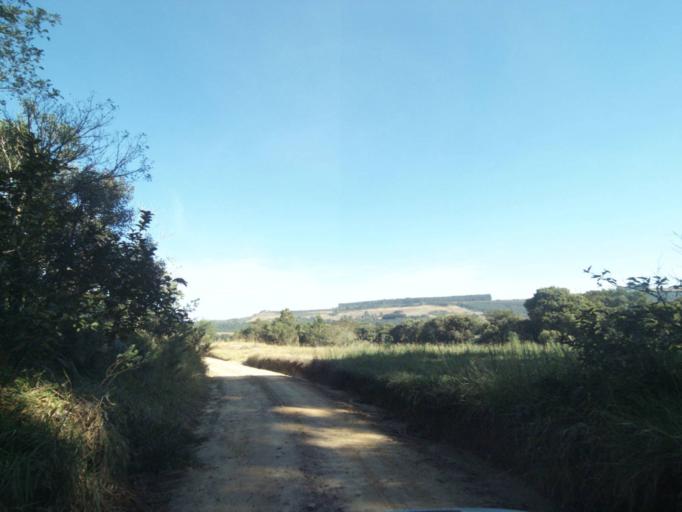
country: BR
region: Parana
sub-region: Tibagi
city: Tibagi
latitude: -24.5592
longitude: -50.4728
